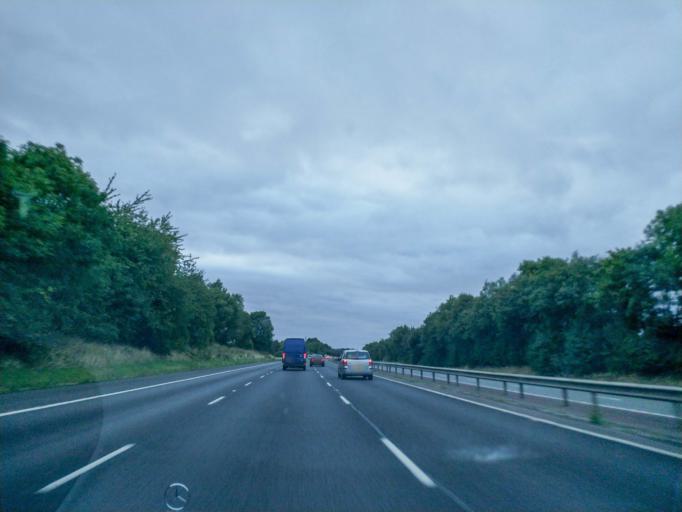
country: GB
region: England
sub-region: Oxfordshire
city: Adderbury
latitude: 52.0244
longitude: -1.2951
